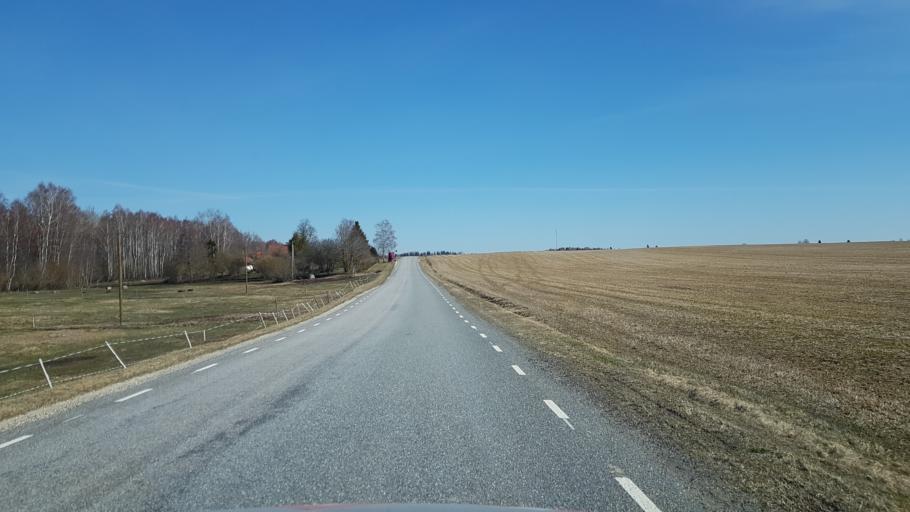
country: EE
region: Laeaene-Virumaa
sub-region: Vinni vald
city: Vinni
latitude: 59.2927
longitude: 26.3919
